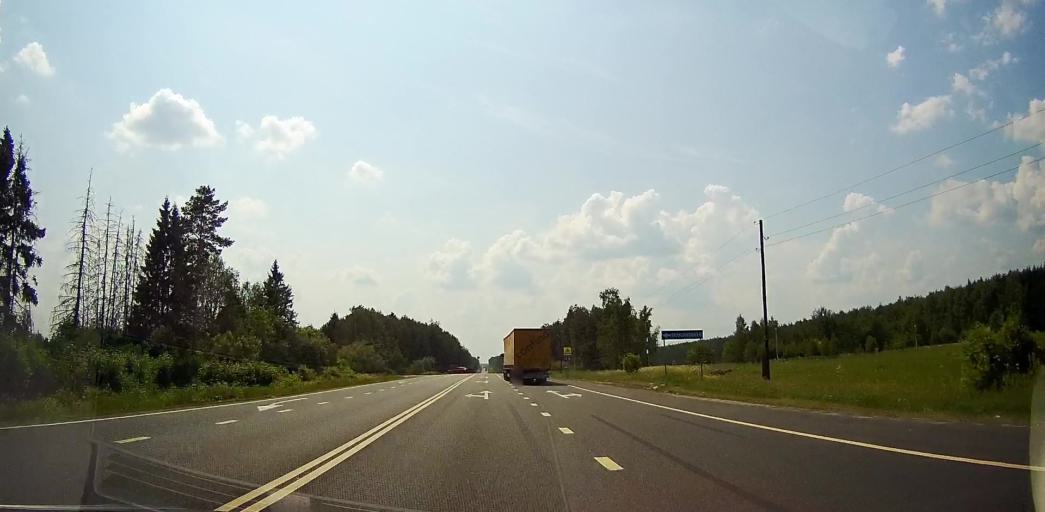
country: RU
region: Moskovskaya
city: Meshcherino
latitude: 55.1739
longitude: 38.3329
